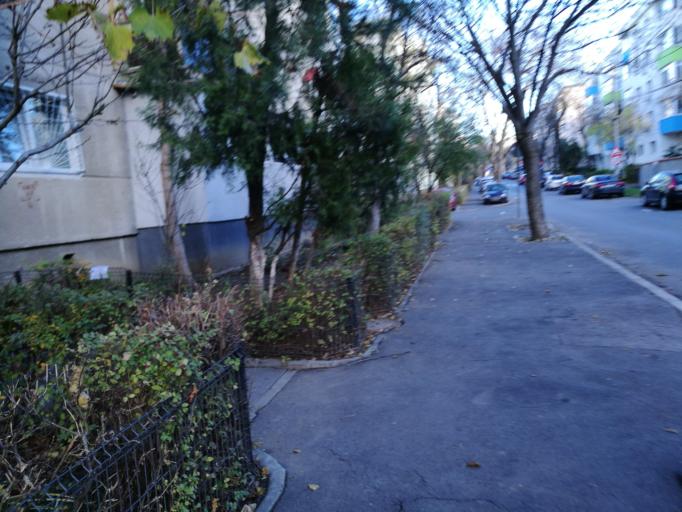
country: RO
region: Ilfov
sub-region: Comuna Otopeni
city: Otopeni
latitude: 44.4908
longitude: 26.0818
